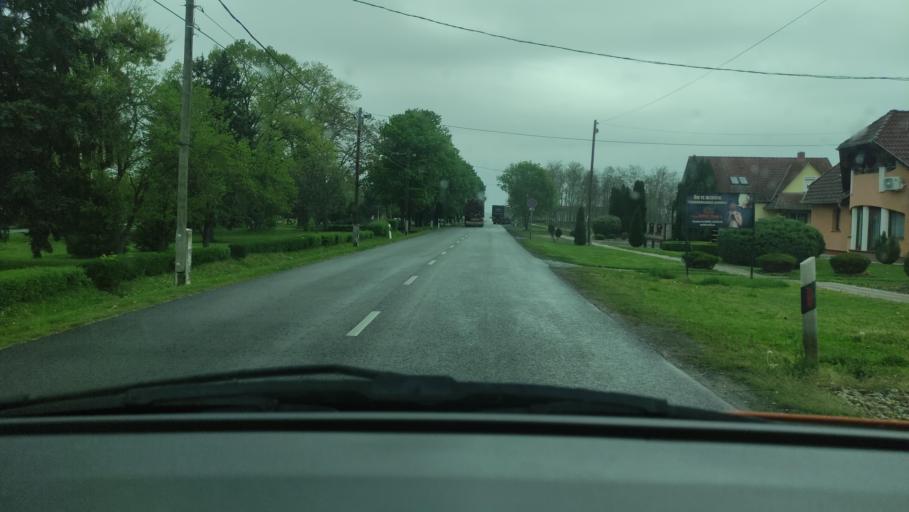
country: HU
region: Baranya
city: Mohacs
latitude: 45.9018
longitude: 18.6602
